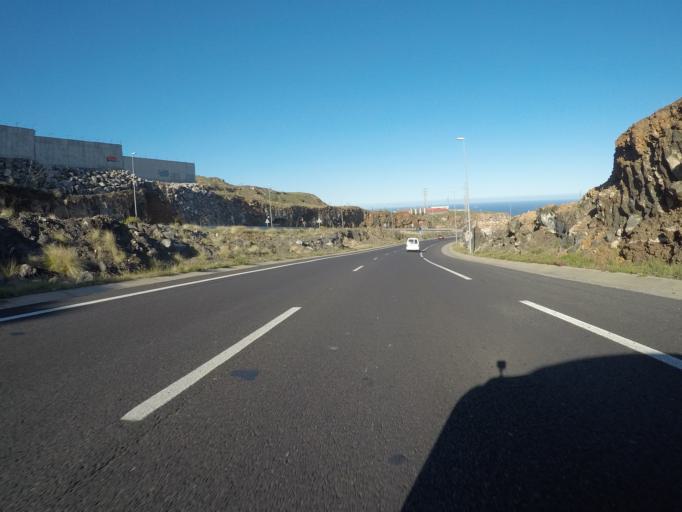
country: ES
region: Canary Islands
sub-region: Provincia de Santa Cruz de Tenerife
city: La Laguna
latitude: 28.4204
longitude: -16.3175
